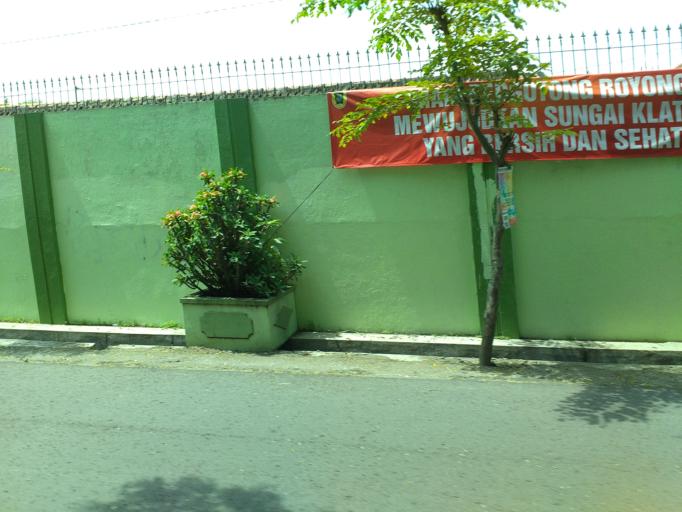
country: ID
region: Central Java
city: Klaten
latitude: -7.7062
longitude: 110.5965
